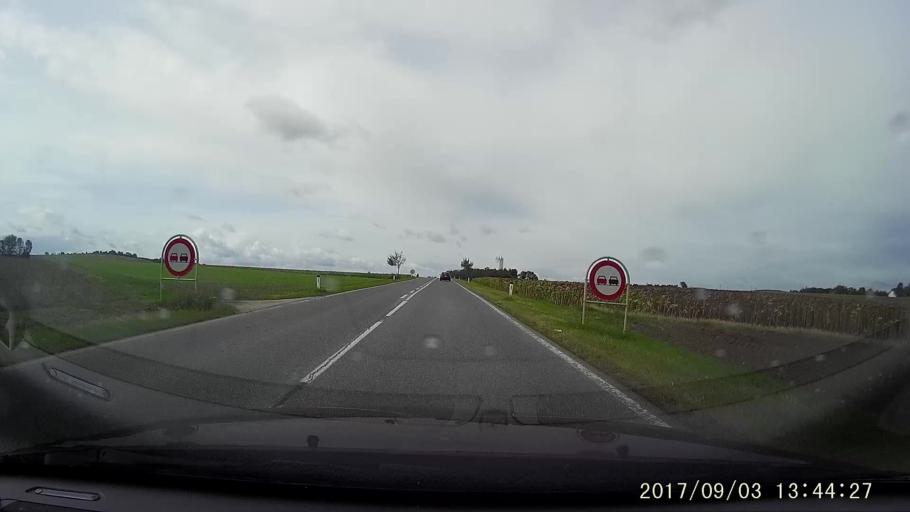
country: AT
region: Lower Austria
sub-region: Politischer Bezirk Hollabrunn
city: Guntersdorf
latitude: 48.6354
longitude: 16.0584
